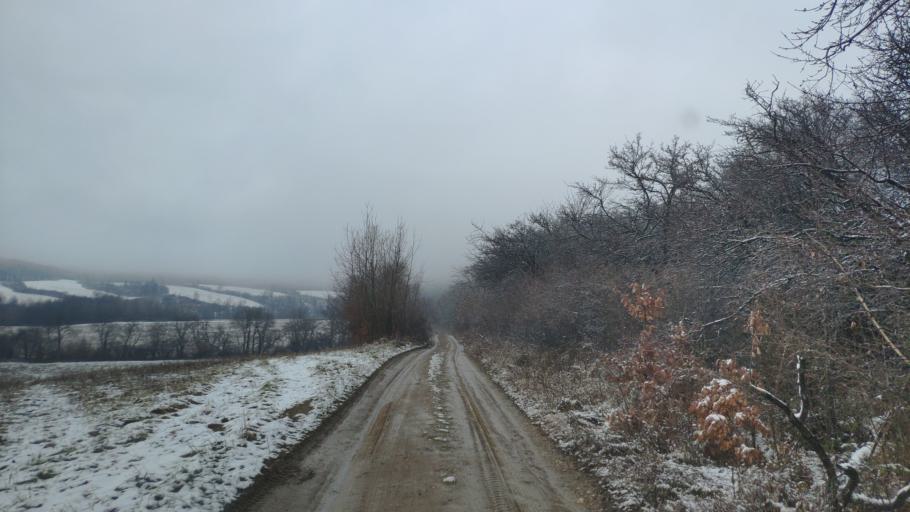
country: SK
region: Kosicky
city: Moldava nad Bodvou
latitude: 48.7368
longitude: 21.0908
